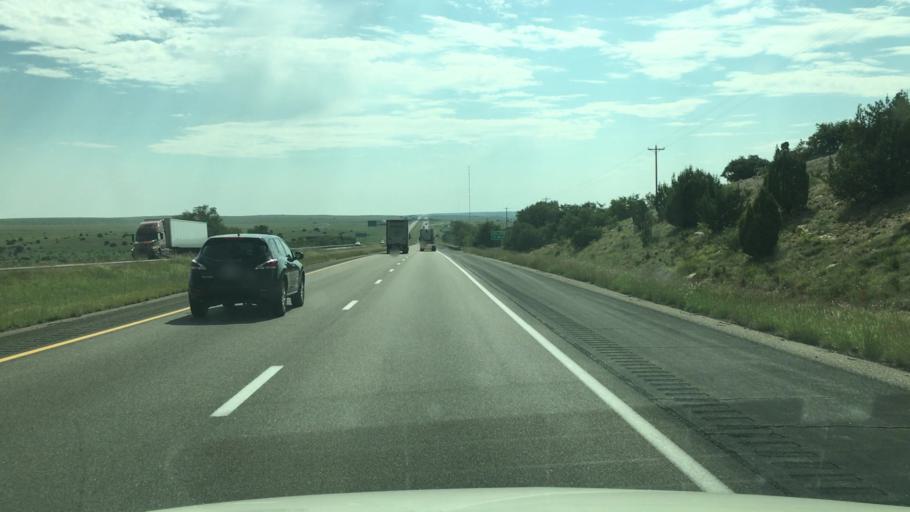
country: US
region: New Mexico
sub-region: San Miguel County
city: Las Vegas
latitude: 34.9924
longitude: -105.3160
